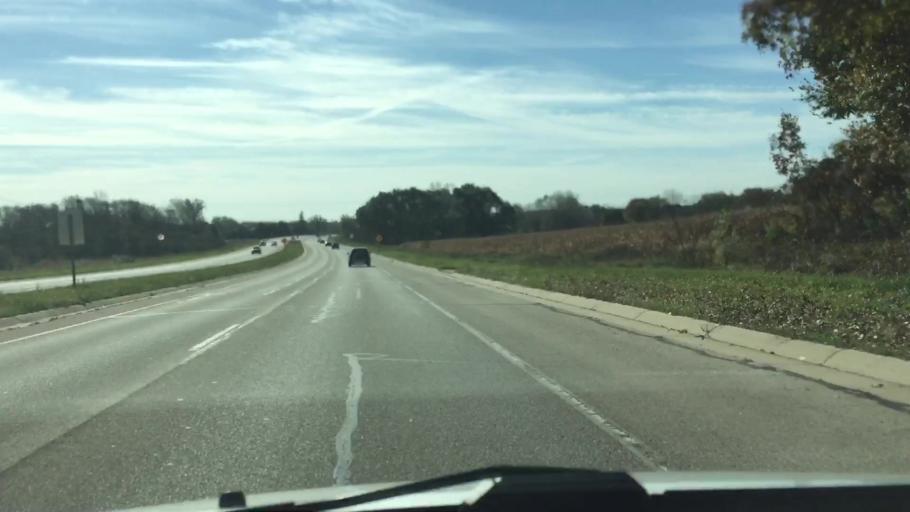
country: US
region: Wisconsin
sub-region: Waukesha County
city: Pewaukee
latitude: 43.1052
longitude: -88.2449
